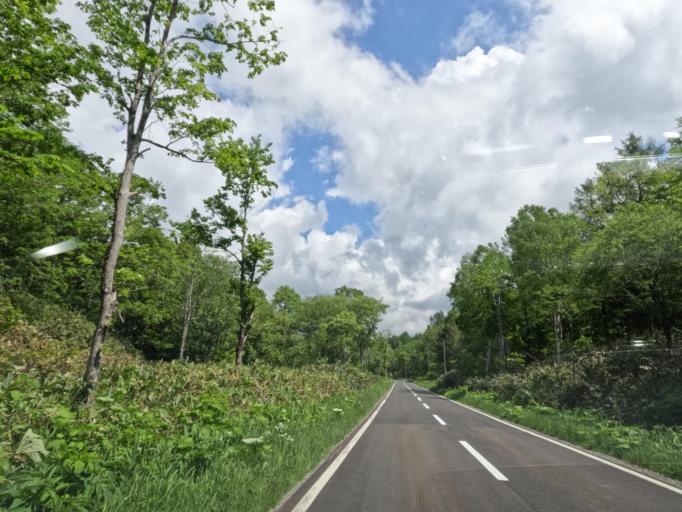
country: JP
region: Hokkaido
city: Takikawa
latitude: 43.5437
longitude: 141.6325
